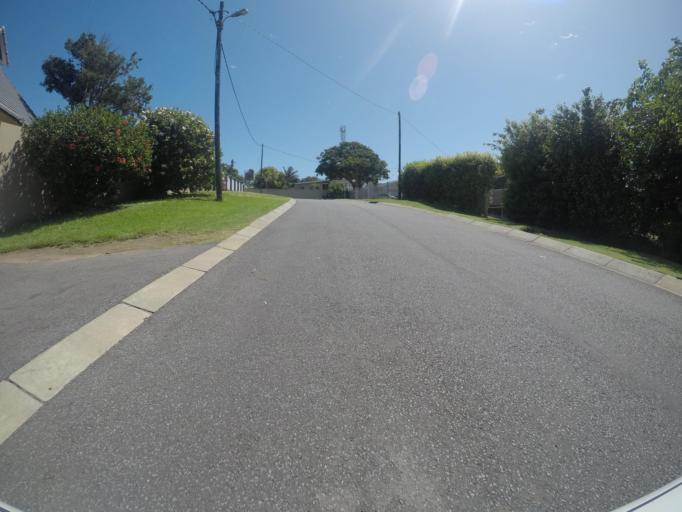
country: ZA
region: Eastern Cape
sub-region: Buffalo City Metropolitan Municipality
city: East London
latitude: -32.9421
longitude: 28.0241
